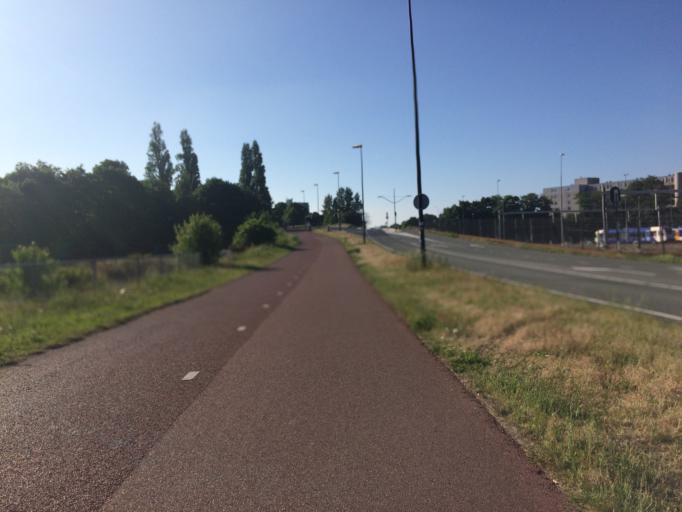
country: NL
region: Gelderland
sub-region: Gemeente Nijmegen
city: Nijmegen
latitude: 51.8344
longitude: 5.8564
